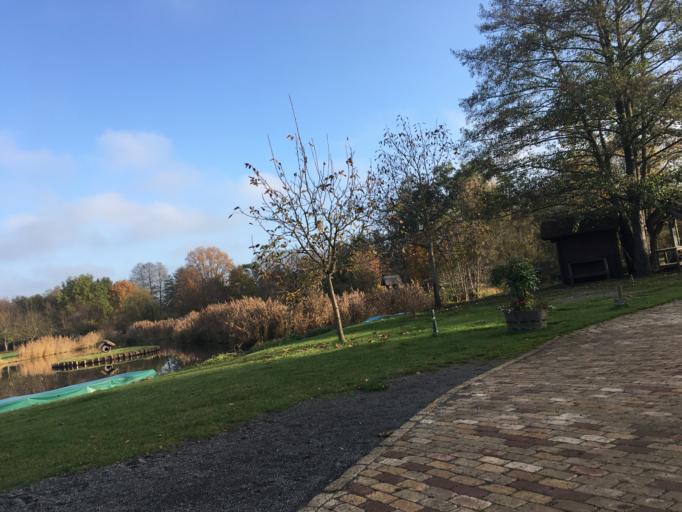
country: DE
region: Brandenburg
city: Schlepzig
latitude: 52.0293
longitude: 13.8884
